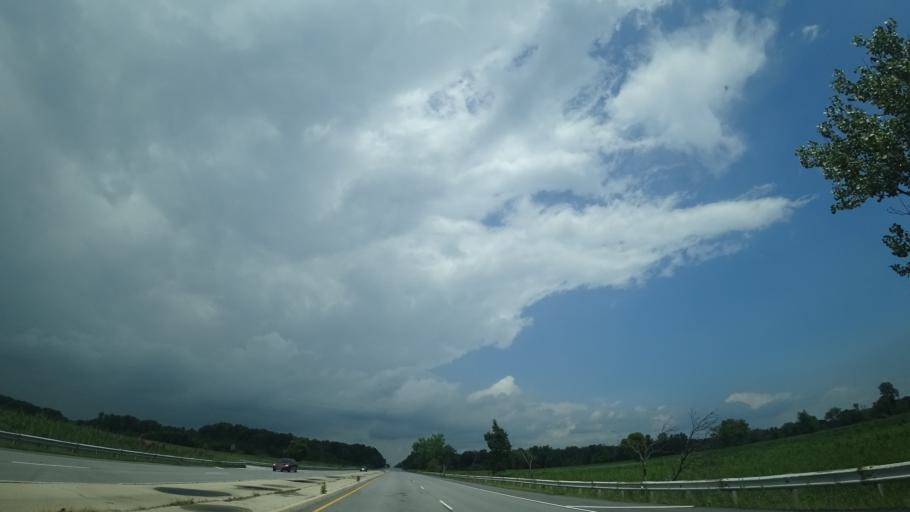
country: US
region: Illinois
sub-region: Cook County
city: Country Club Hills
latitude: 41.5361
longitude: -87.7326
